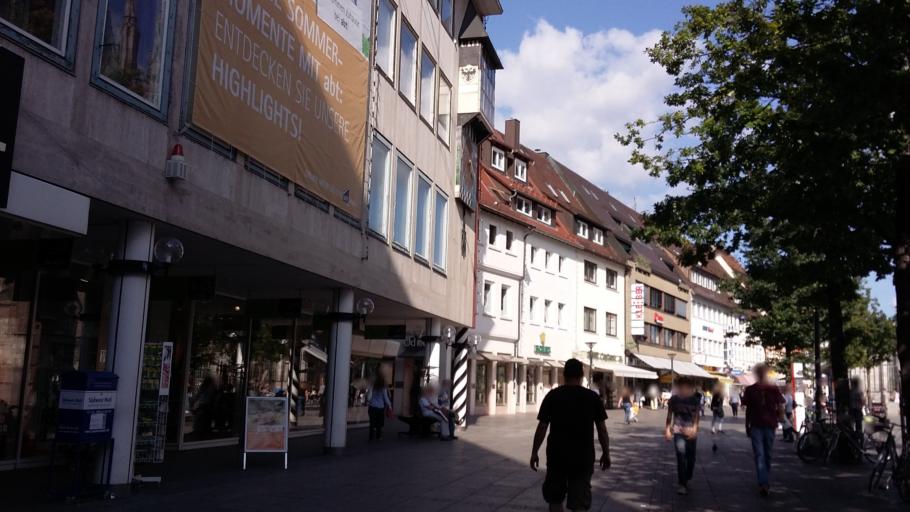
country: DE
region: Baden-Wuerttemberg
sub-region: Tuebingen Region
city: Ulm
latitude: 48.3989
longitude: 9.9906
